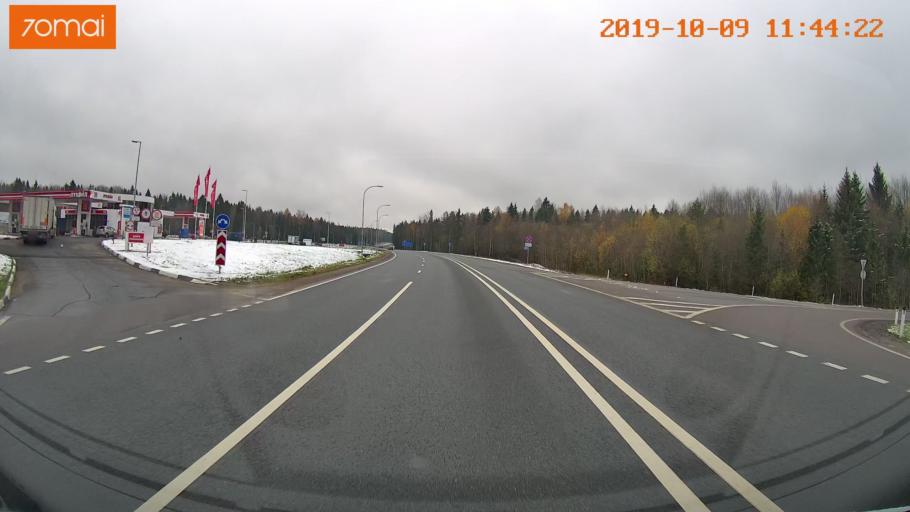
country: RU
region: Vologda
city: Gryazovets
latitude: 58.8842
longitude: 40.1903
